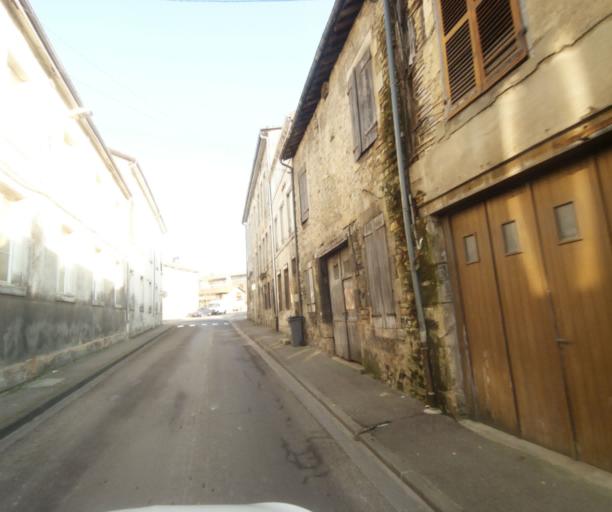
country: FR
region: Champagne-Ardenne
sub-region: Departement de la Haute-Marne
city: Wassy
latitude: 48.4997
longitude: 4.9482
